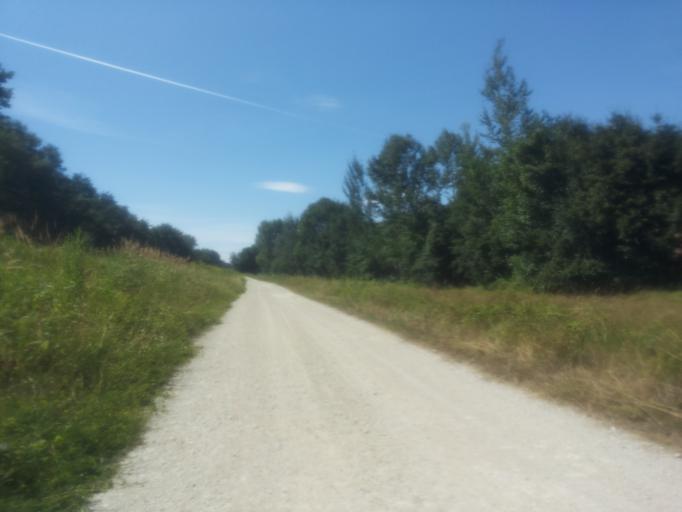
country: DE
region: Bavaria
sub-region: Upper Bavaria
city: Grossmehring
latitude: 48.7596
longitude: 11.5045
